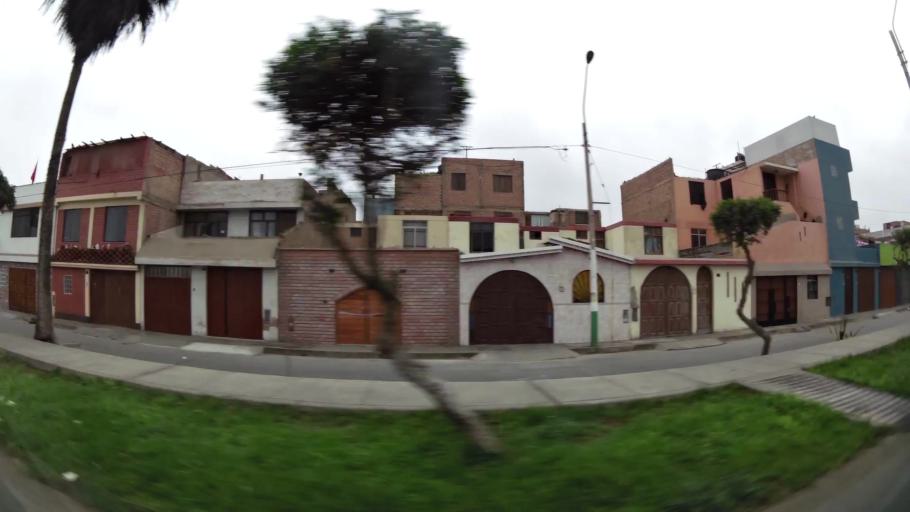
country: PE
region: Callao
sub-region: Callao
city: Callao
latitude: -12.0754
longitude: -77.1157
